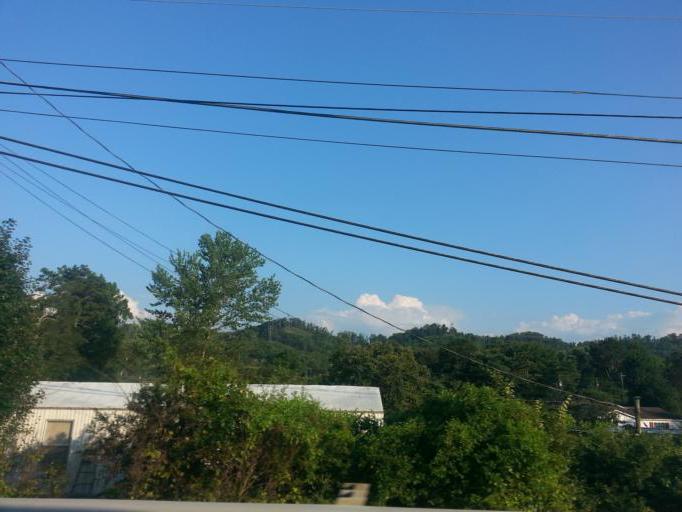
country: US
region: Tennessee
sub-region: Anderson County
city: Clinton
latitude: 36.0329
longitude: -84.1389
